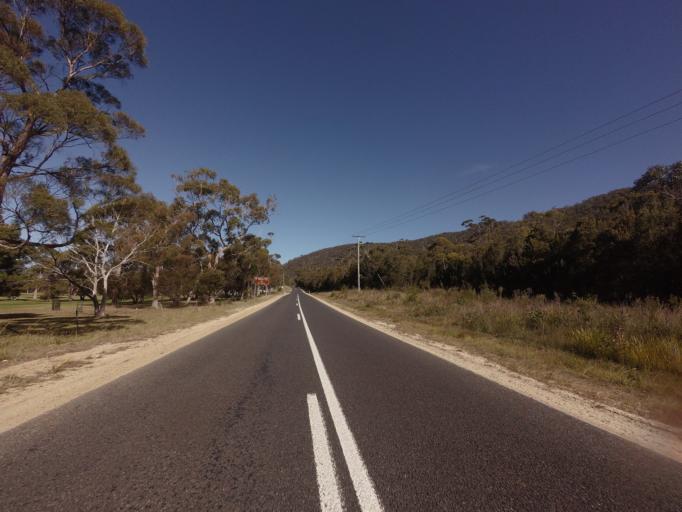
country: AU
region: Tasmania
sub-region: Break O'Day
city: St Helens
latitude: -41.8509
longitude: 148.2628
